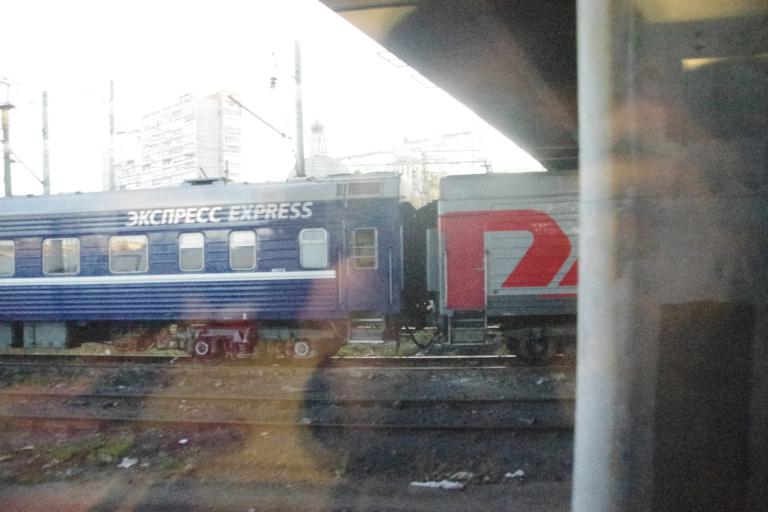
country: RU
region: Moscow
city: Mar'ina Roshcha
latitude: 55.7925
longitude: 37.6415
